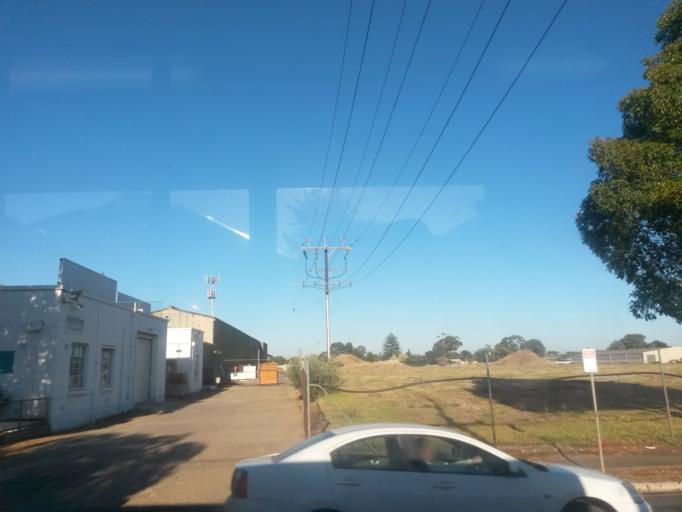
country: AU
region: South Australia
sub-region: Charles Sturt
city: Woodville
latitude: -34.8781
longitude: 138.5665
